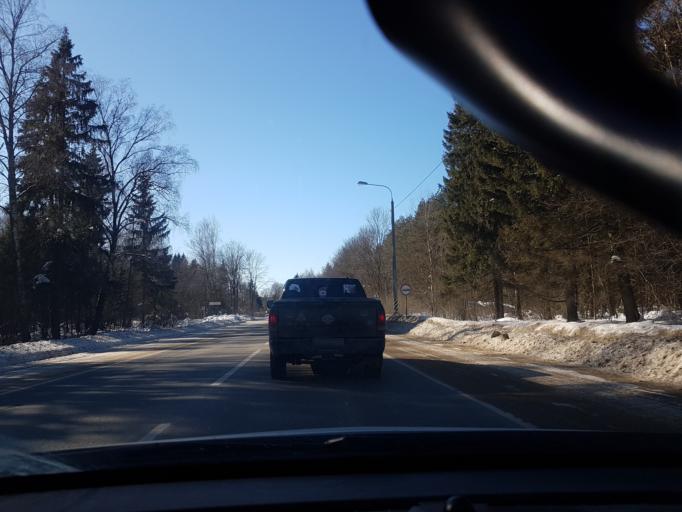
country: RU
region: Moskovskaya
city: Kostrovo
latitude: 55.9138
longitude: 36.7400
